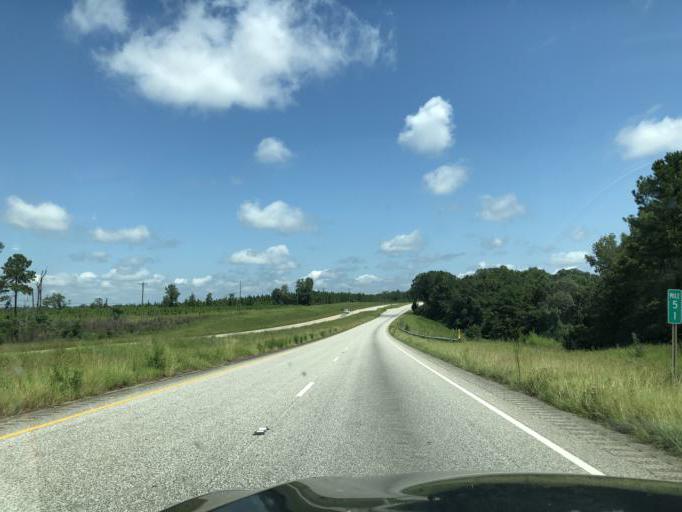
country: US
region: Alabama
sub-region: Henry County
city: Abbeville
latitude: 31.7127
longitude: -85.2730
